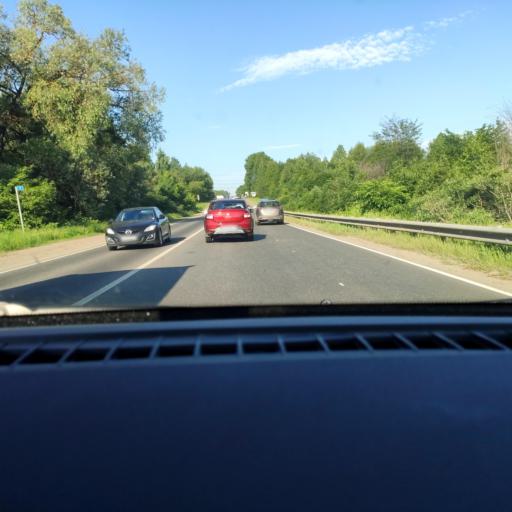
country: RU
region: Udmurtiya
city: Khokhryaki
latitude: 56.9131
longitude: 53.3857
